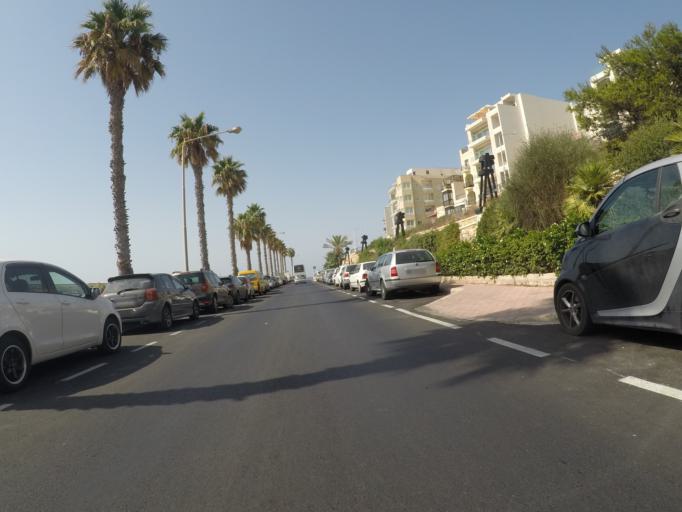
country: MT
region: Saint Paul's Bay
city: San Pawl il-Bahar
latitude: 35.9505
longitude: 14.4088
